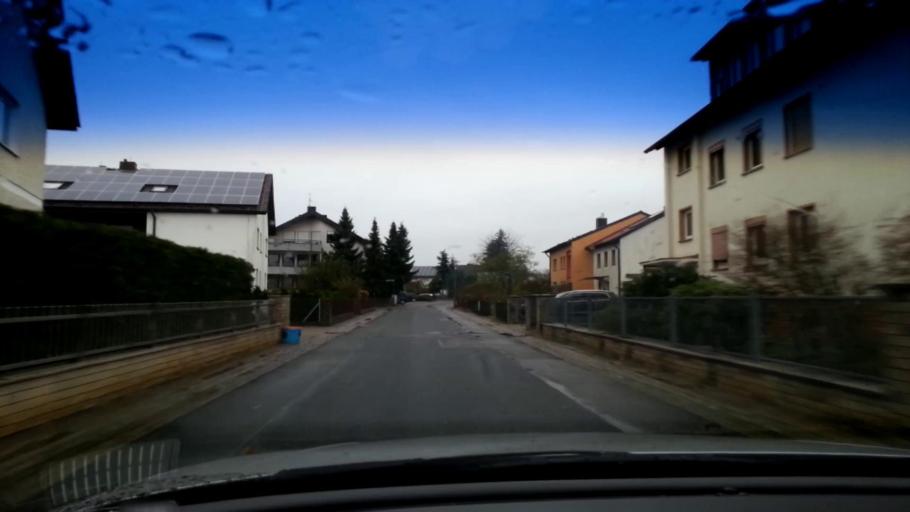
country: DE
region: Bavaria
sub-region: Upper Franconia
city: Hallstadt
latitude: 49.9248
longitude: 10.8843
